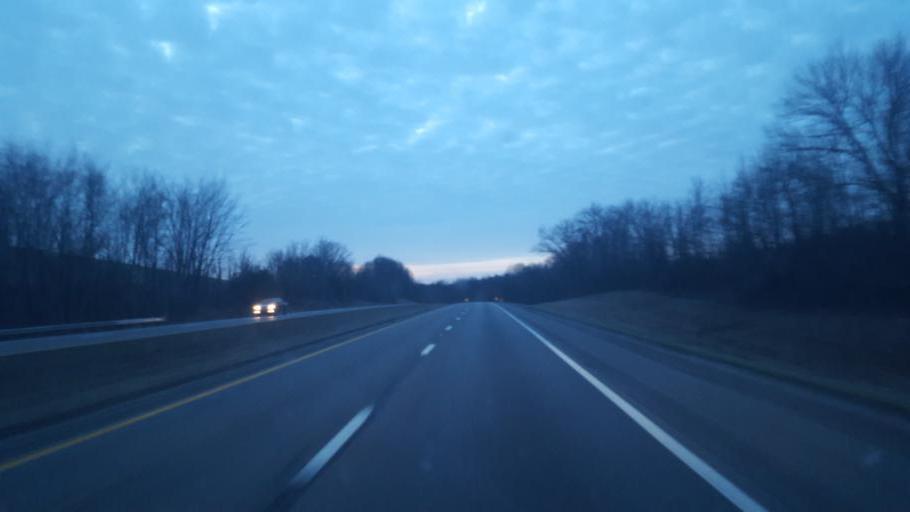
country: US
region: Ohio
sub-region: Jackson County
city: Oak Hill
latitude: 38.9809
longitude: -82.5261
